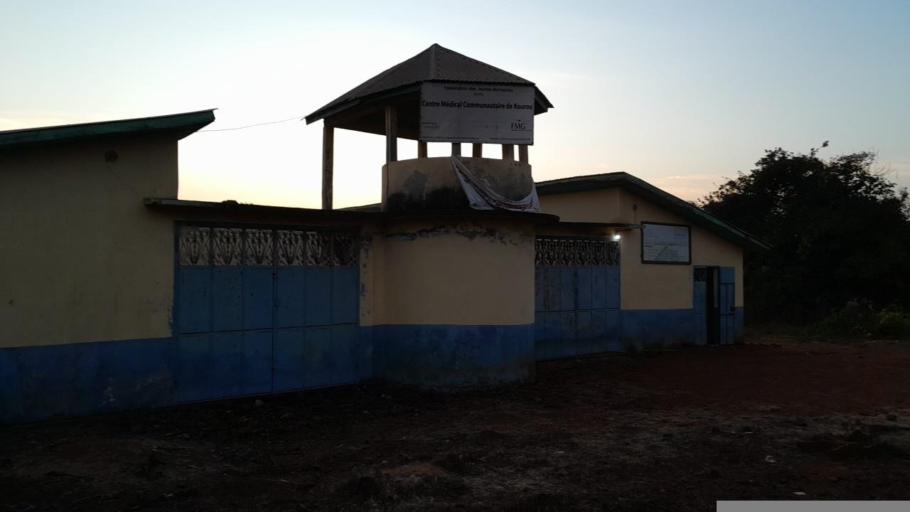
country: GN
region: Mamou
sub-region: Pita
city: Pita
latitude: 11.1681
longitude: -12.6177
